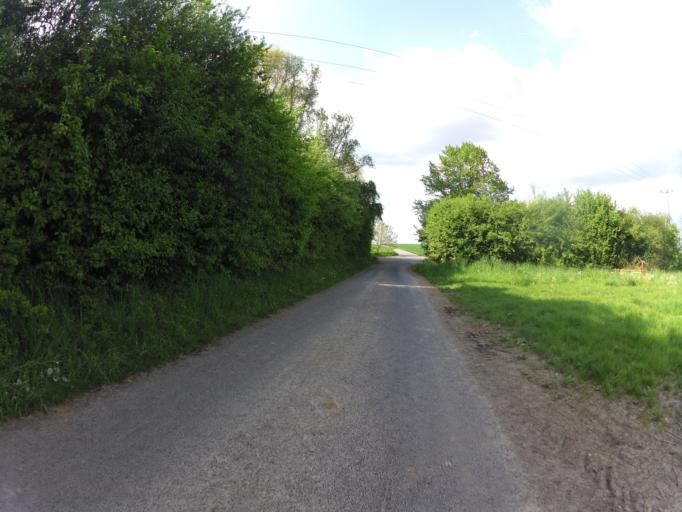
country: DE
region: Bavaria
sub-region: Regierungsbezirk Unterfranken
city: Giebelstadt
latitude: 49.6338
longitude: 9.9410
